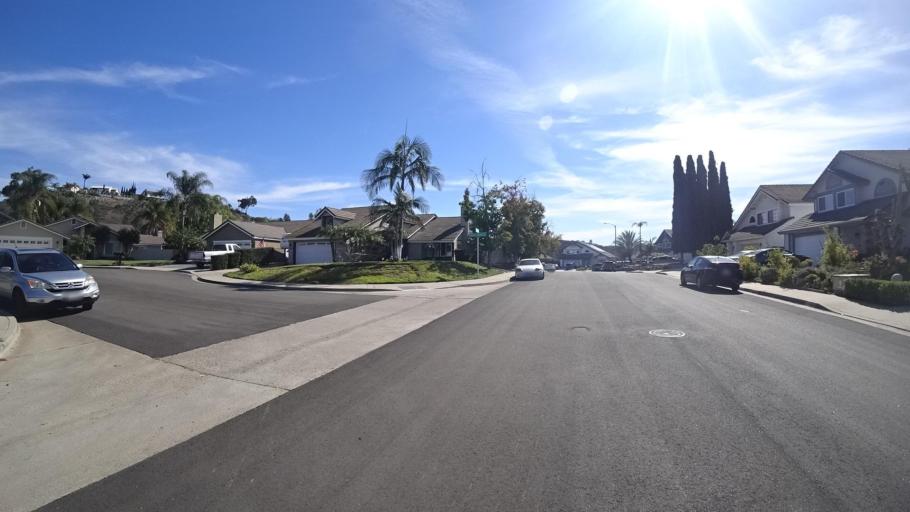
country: US
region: California
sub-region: San Diego County
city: Casa de Oro-Mount Helix
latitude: 32.7481
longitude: -116.9559
